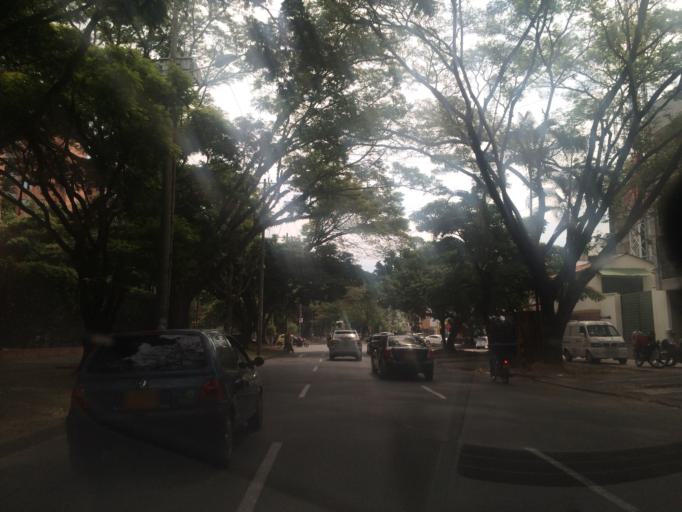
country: CO
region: Valle del Cauca
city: Cali
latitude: 3.3803
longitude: -76.5259
